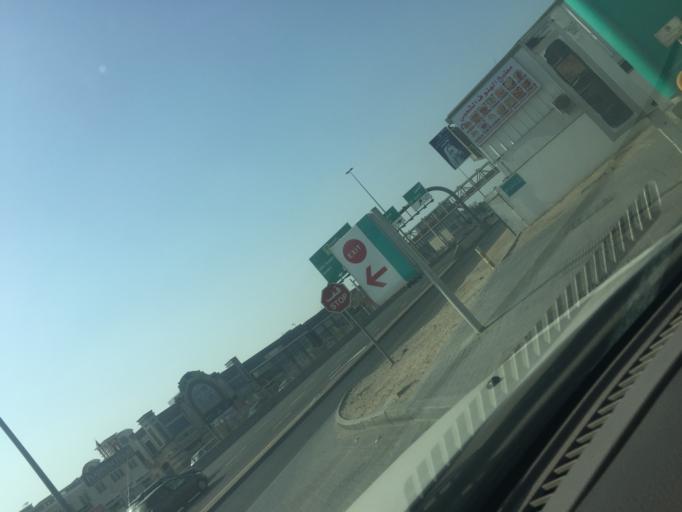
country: AE
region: Dubai
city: Dubai
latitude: 25.1064
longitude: 55.2276
